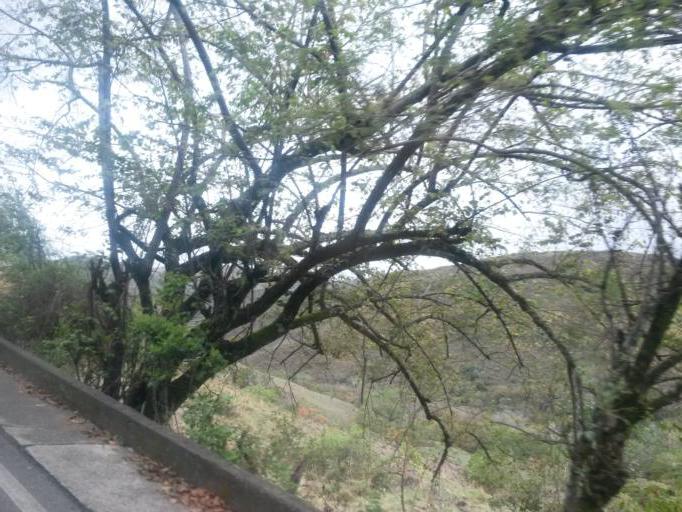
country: CO
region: Cauca
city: El Bordo
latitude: 2.1715
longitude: -76.8949
